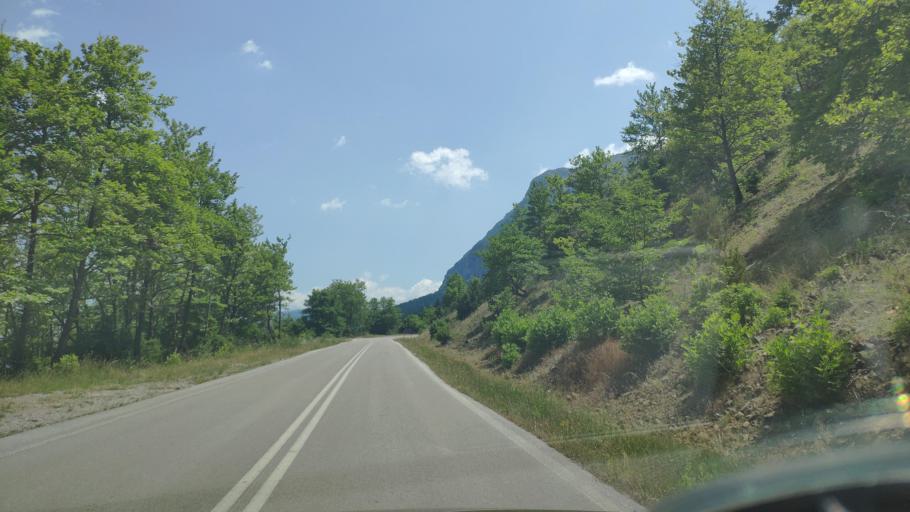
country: GR
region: Epirus
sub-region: Nomos Artas
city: Ano Kalentini
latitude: 39.2765
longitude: 21.2908
